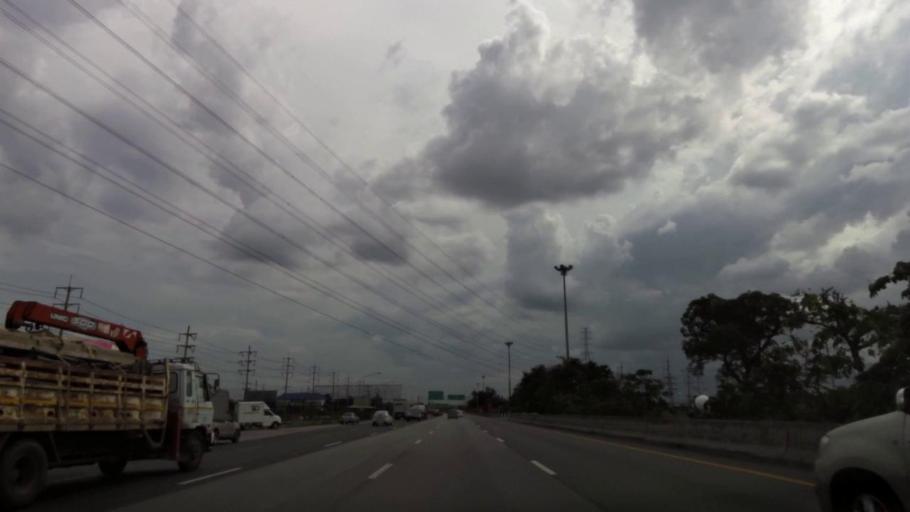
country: TH
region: Phra Nakhon Si Ayutthaya
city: Bang Pa-in
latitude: 14.1841
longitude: 100.6133
